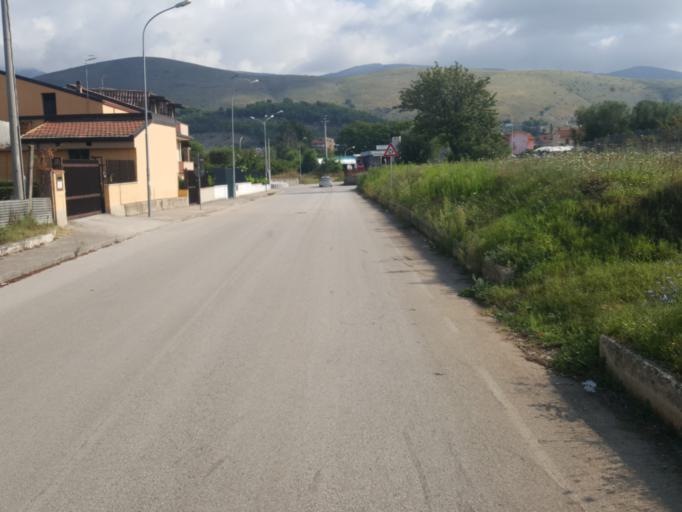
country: IT
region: Campania
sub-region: Provincia di Caserta
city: Pignataro Maggiore
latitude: 41.1878
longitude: 14.1635
